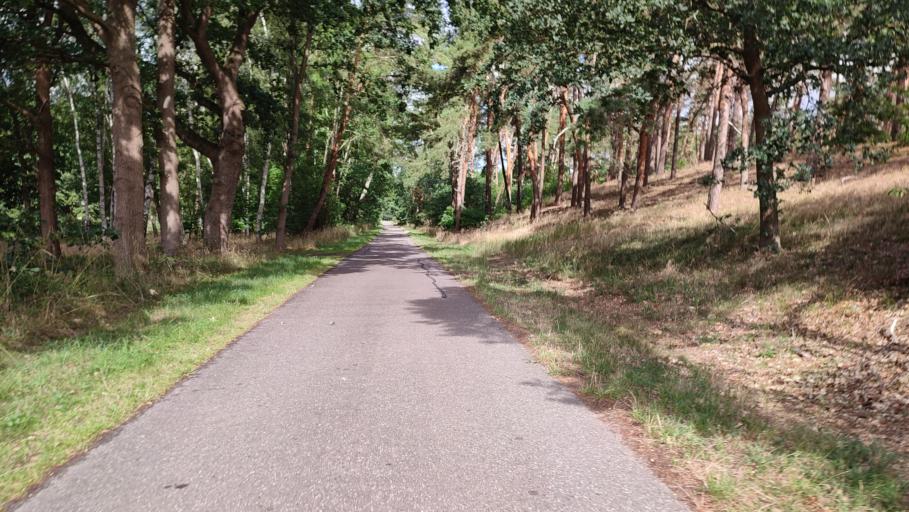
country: DE
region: Lower Saxony
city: Neu Darchau
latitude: 53.2331
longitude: 10.9761
